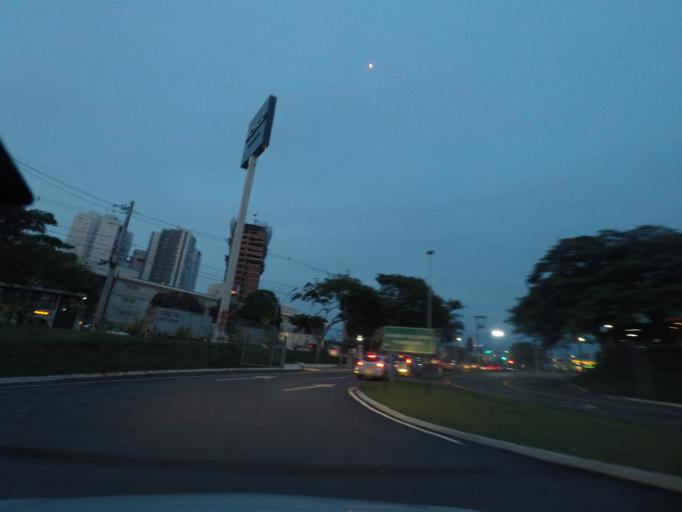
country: BR
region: Goias
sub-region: Goiania
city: Goiania
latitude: -16.7083
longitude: -49.2363
